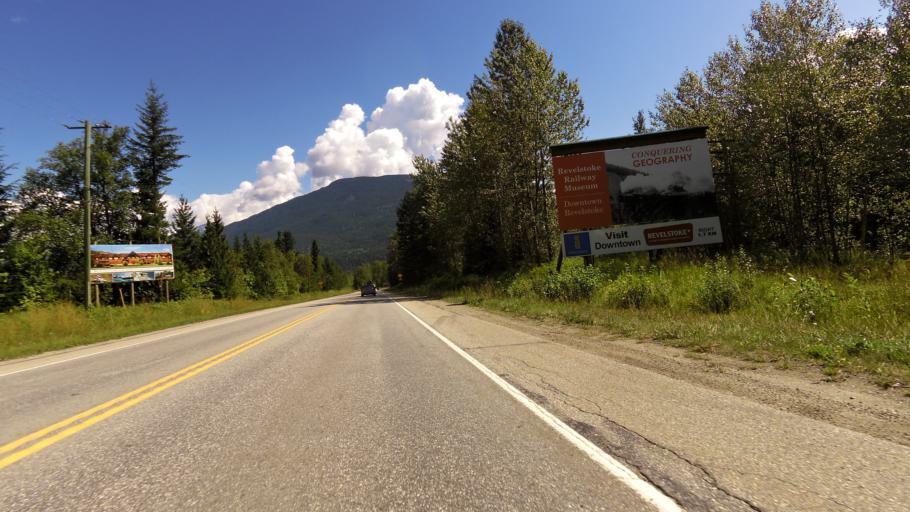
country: CA
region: British Columbia
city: Revelstoke
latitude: 51.0010
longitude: -118.2361
